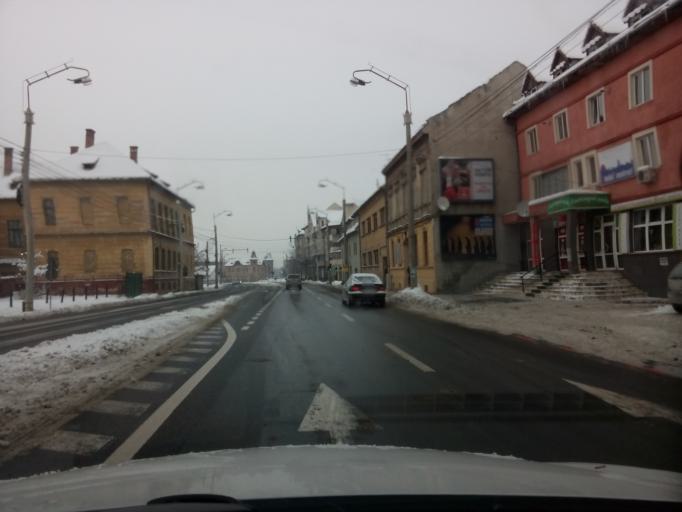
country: RO
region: Sibiu
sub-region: Municipiul Sibiu
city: Sibiu
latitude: 45.7991
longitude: 24.1574
